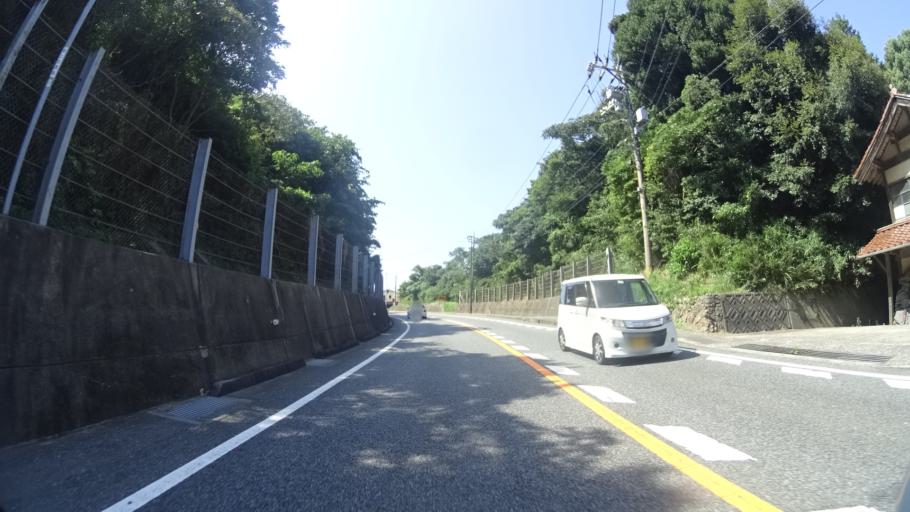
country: JP
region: Shimane
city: Masuda
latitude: 34.7481
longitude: 131.8739
